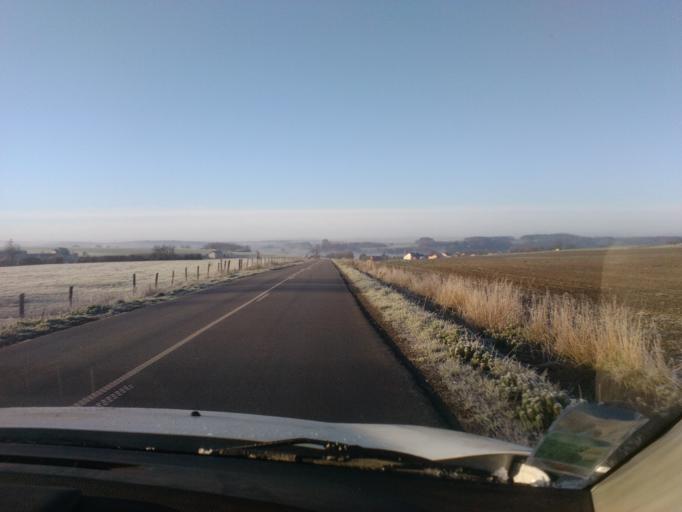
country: FR
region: Lorraine
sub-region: Departement des Vosges
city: Darnieulles
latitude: 48.1890
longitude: 6.2246
